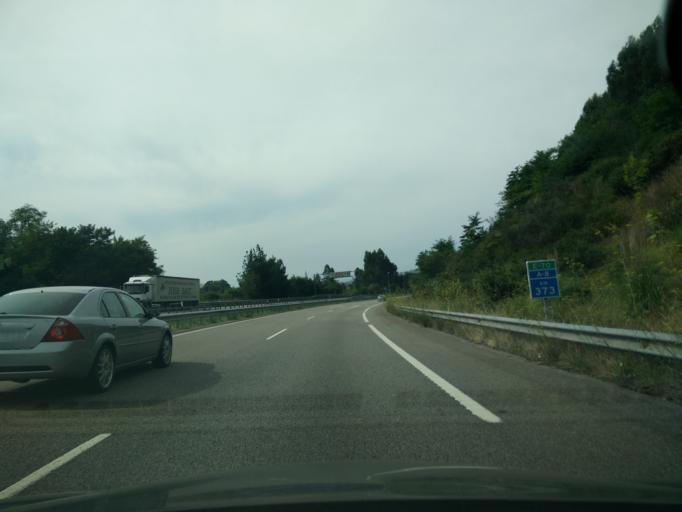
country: ES
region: Asturias
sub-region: Province of Asturias
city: Arriba
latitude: 43.5054
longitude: -5.5936
